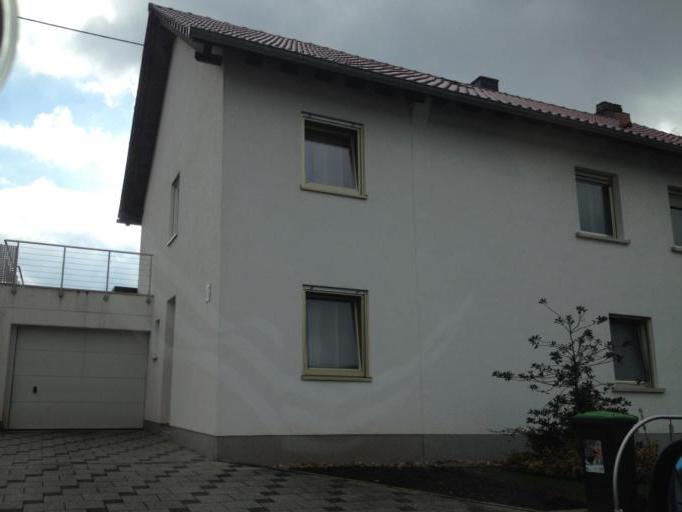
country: DE
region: Saarland
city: Bexbach
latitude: 49.3263
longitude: 7.2184
